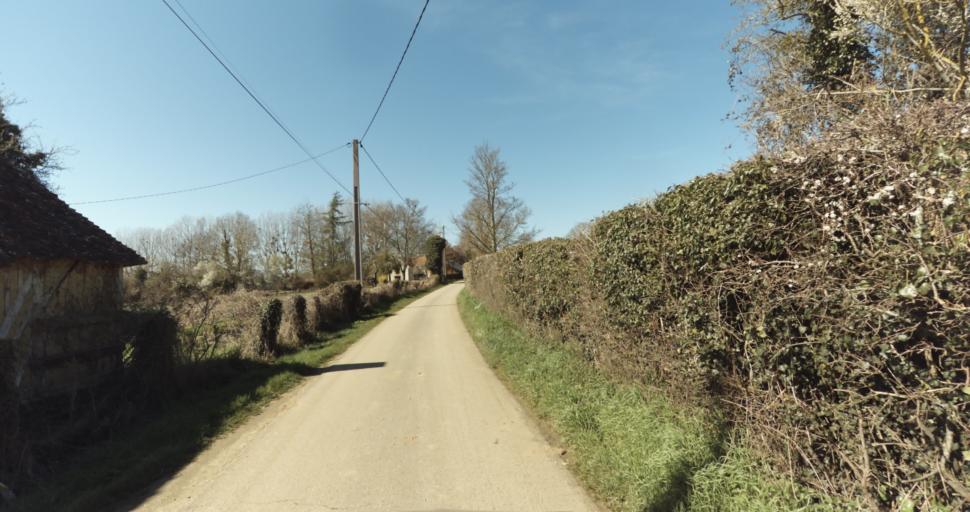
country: FR
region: Lower Normandy
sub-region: Departement du Calvados
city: Saint-Pierre-sur-Dives
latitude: 49.0669
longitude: -0.0328
